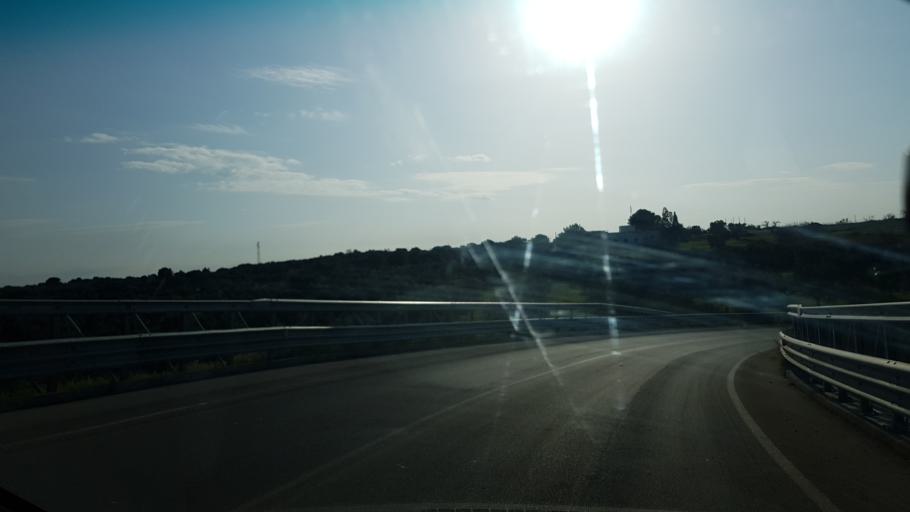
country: IT
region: Apulia
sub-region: Provincia di Brindisi
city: San Vito dei Normanni
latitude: 40.6844
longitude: 17.7772
